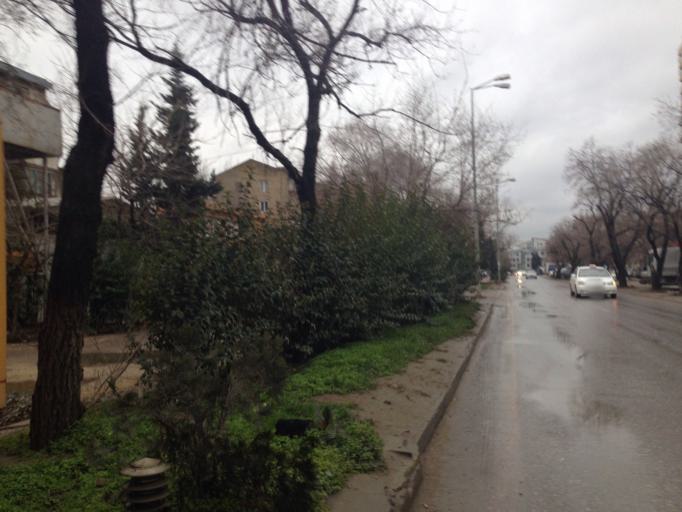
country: AZ
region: Baki
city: Baku
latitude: 40.4104
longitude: 49.8682
